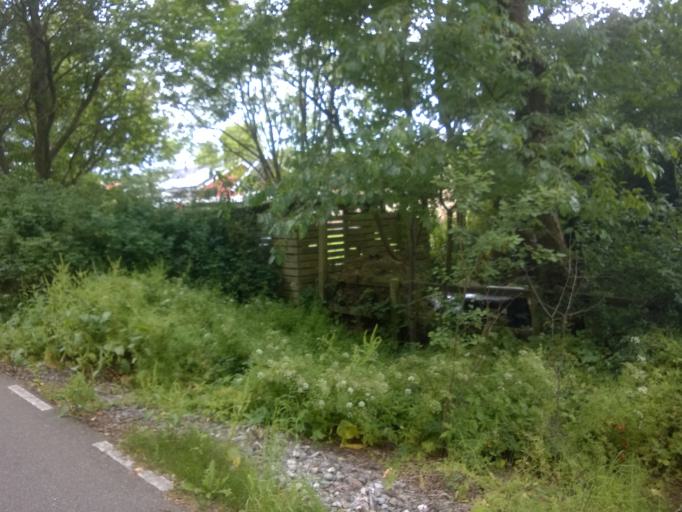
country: DK
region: Central Jutland
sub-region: Silkeborg Kommune
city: Svejbaek
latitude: 56.1703
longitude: 9.6126
